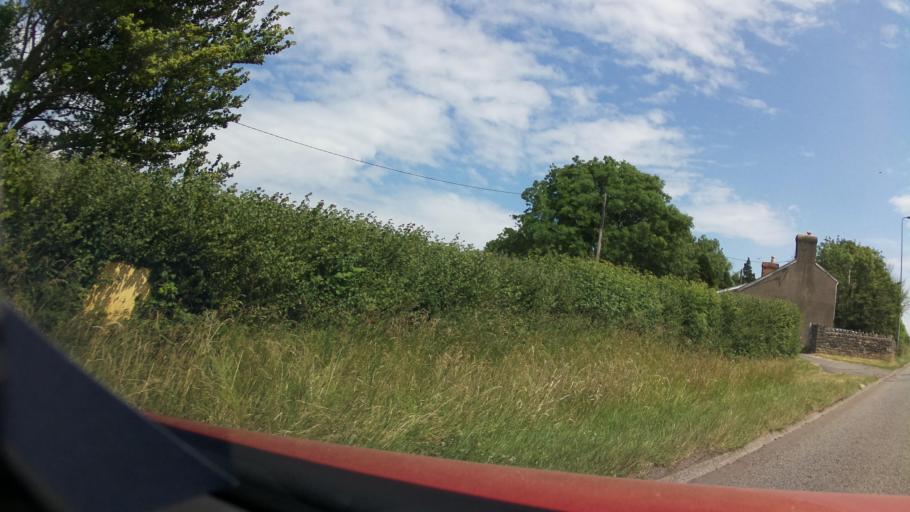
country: GB
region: Wales
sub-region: Vale of Glamorgan
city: Llangan
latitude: 51.4803
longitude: -3.5280
